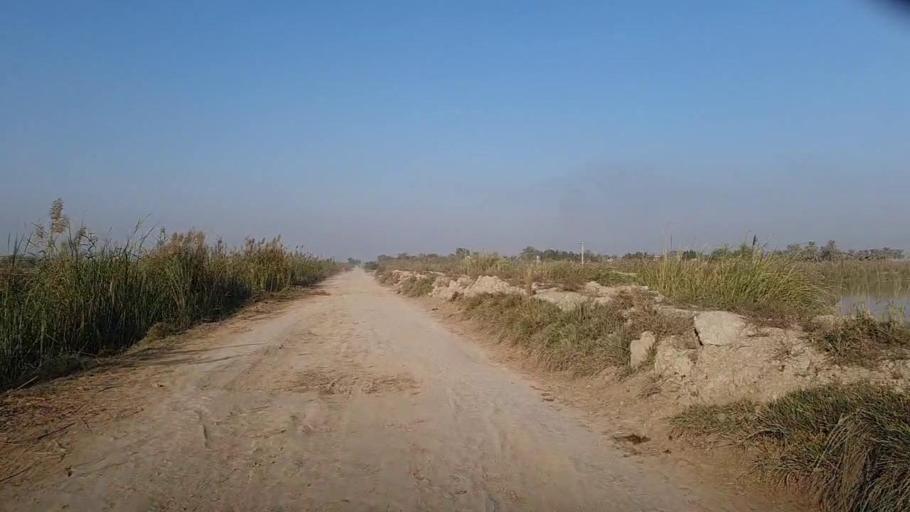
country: PK
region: Sindh
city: Ranipur
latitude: 27.2558
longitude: 68.5097
